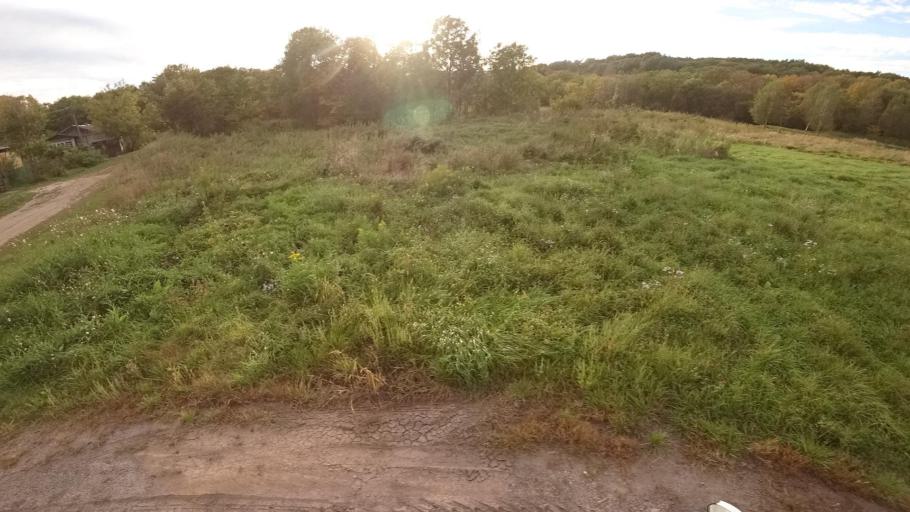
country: RU
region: Primorskiy
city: Yakovlevka
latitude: 44.4188
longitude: 133.4468
